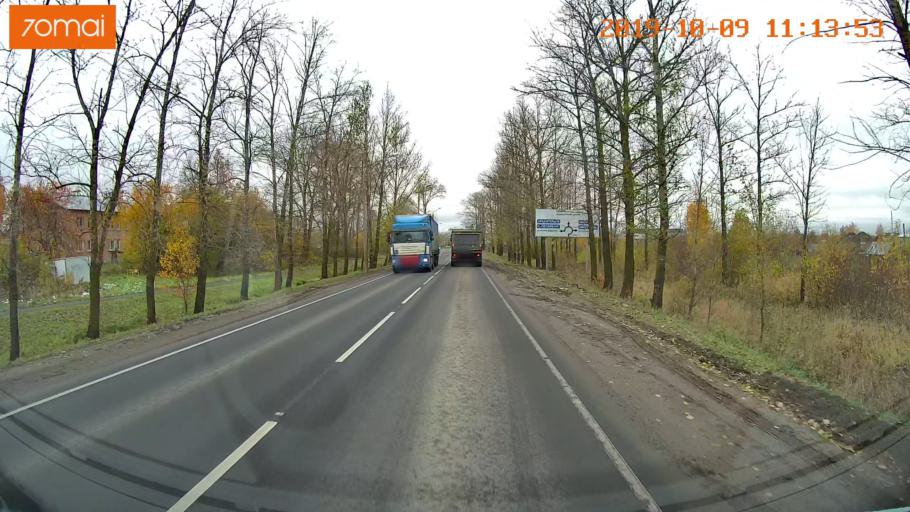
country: RU
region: Vologda
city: Vologda
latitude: 59.1849
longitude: 39.8480
